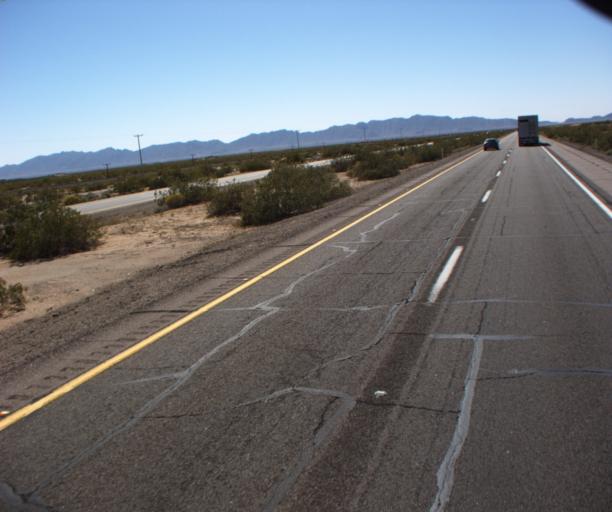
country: US
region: Arizona
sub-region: Yuma County
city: Wellton
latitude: 32.7802
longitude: -113.5848
